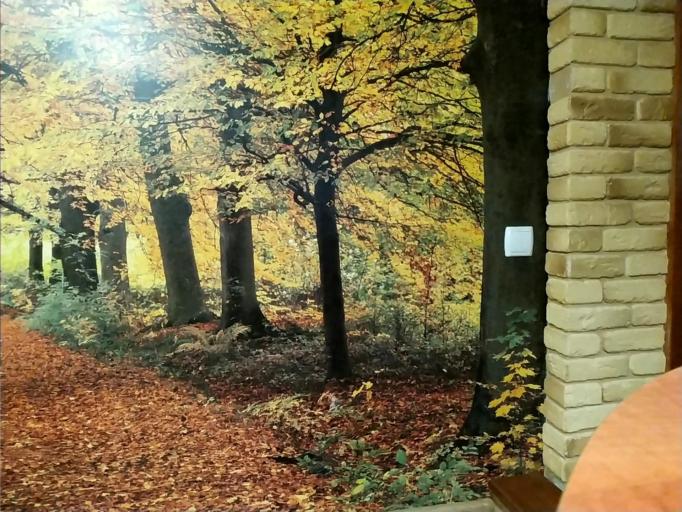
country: BY
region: Minsk
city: Il'ya
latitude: 54.4254
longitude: 27.5537
